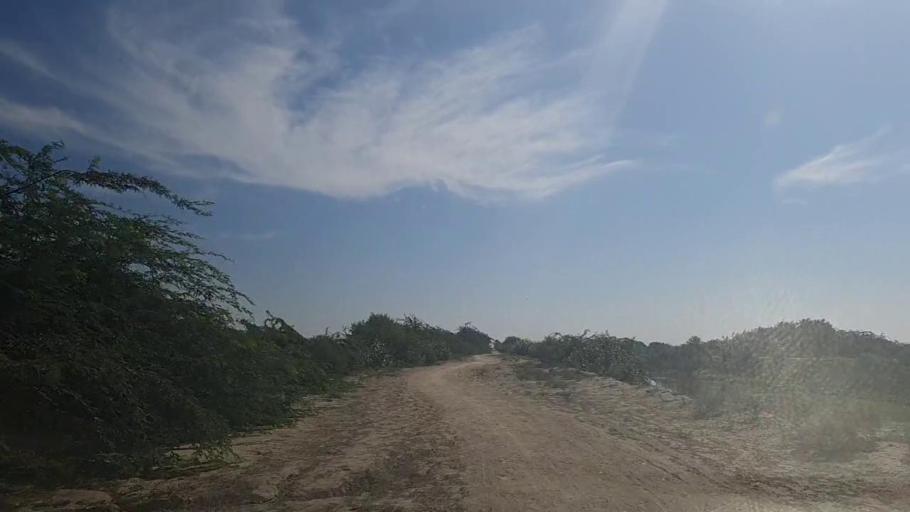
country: PK
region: Sindh
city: Mirpur Batoro
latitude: 24.6572
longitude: 68.1979
